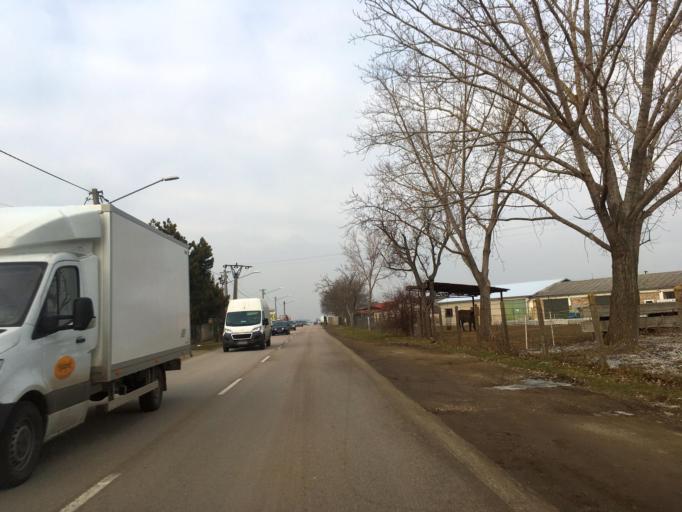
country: SK
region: Nitriansky
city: Sellye
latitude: 48.1747
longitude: 17.8616
